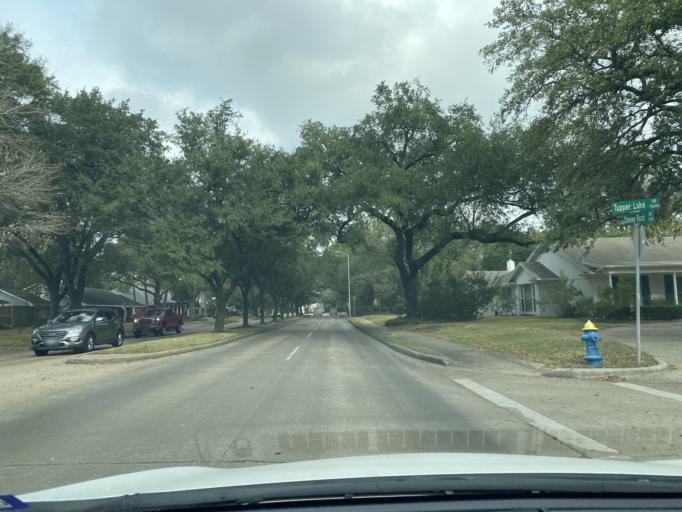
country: US
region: Texas
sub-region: Harris County
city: Hunters Creek Village
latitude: 29.7601
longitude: -95.4773
